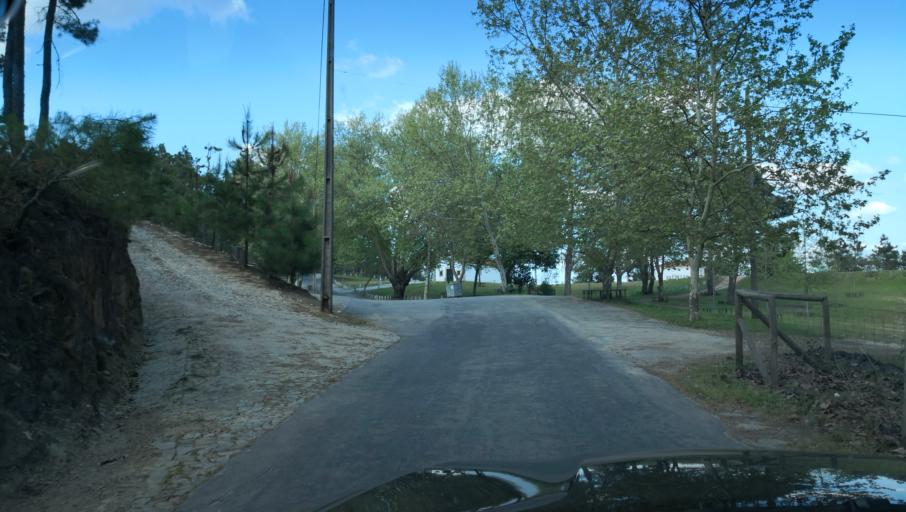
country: PT
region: Vila Real
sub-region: Sabrosa
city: Vilela
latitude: 41.2315
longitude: -7.6704
